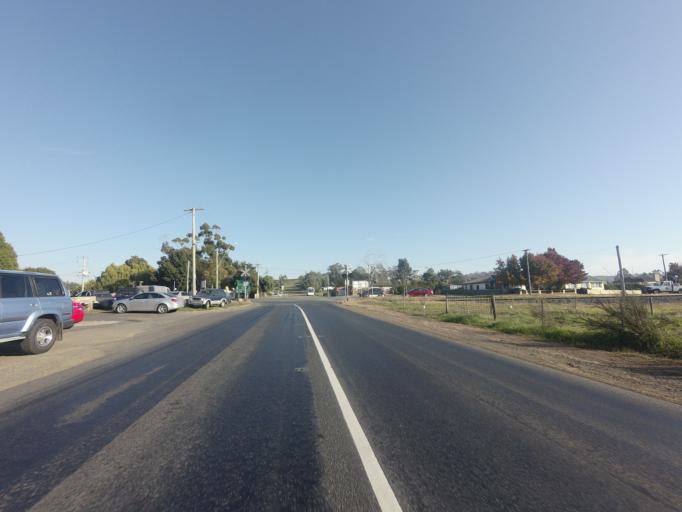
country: AU
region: Tasmania
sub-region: Northern Midlands
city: Perth
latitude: -41.5766
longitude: 147.1618
